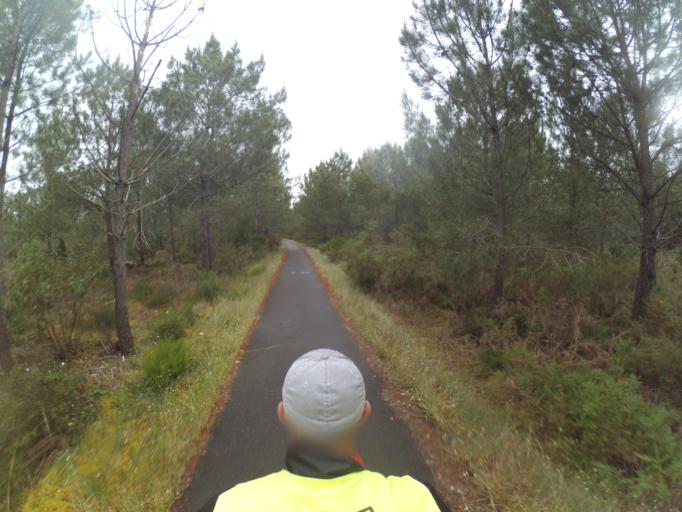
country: FR
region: Aquitaine
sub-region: Departement des Landes
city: Mimizan
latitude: 44.2240
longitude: -1.2594
